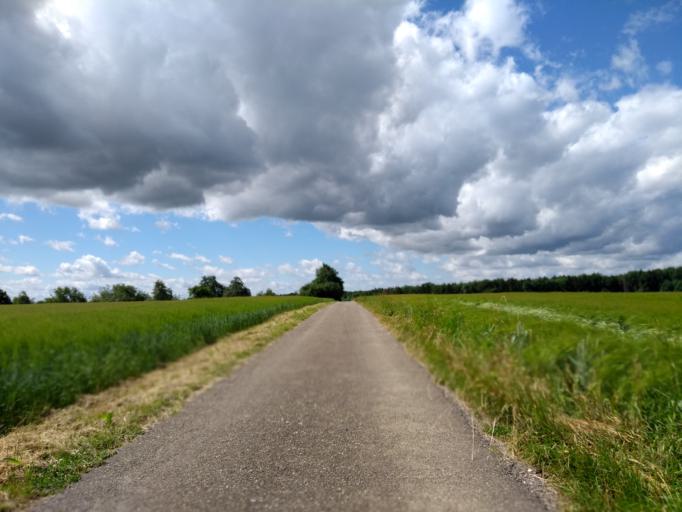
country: DE
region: Baden-Wuerttemberg
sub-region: Tuebingen Region
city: Mehrstetten
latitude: 48.3432
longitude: 9.6364
